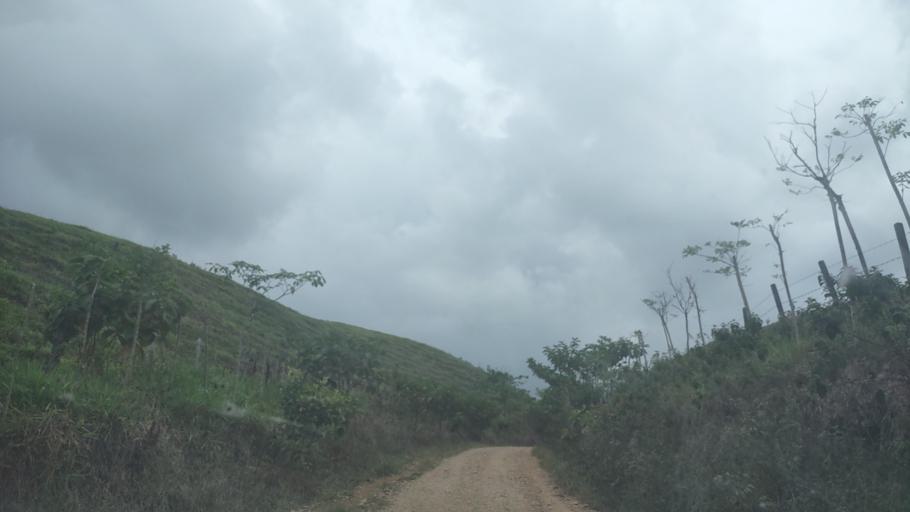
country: MX
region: Tabasco
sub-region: Huimanguillo
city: Francisco Rueda
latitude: 17.4405
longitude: -94.0285
